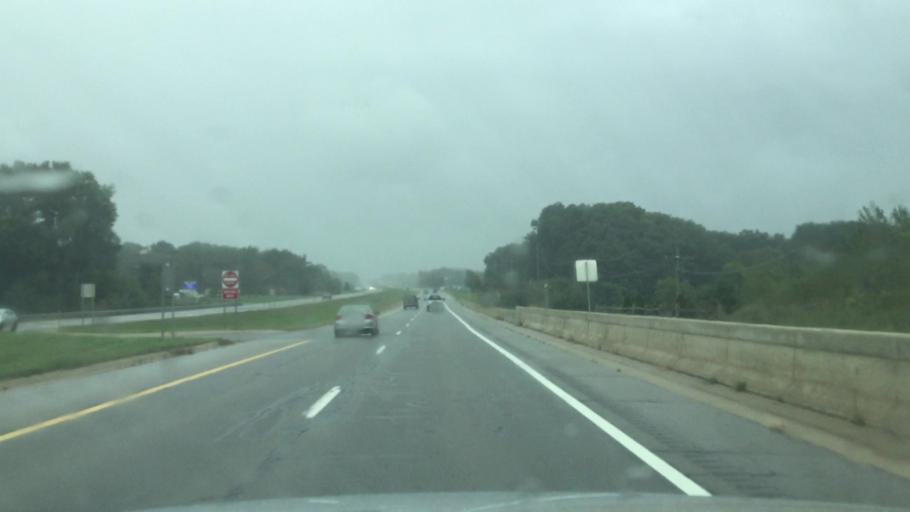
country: US
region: Michigan
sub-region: Livingston County
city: Howell
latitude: 42.6219
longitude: -83.9664
